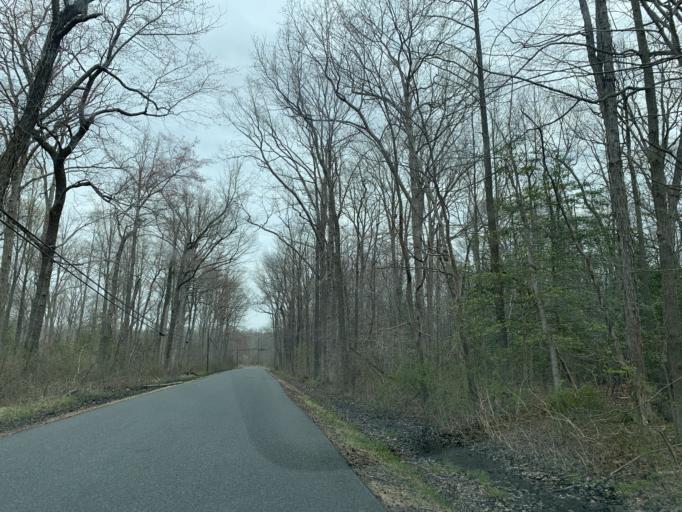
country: US
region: Maryland
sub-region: Baltimore County
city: Edgemere
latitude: 39.2640
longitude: -76.4220
